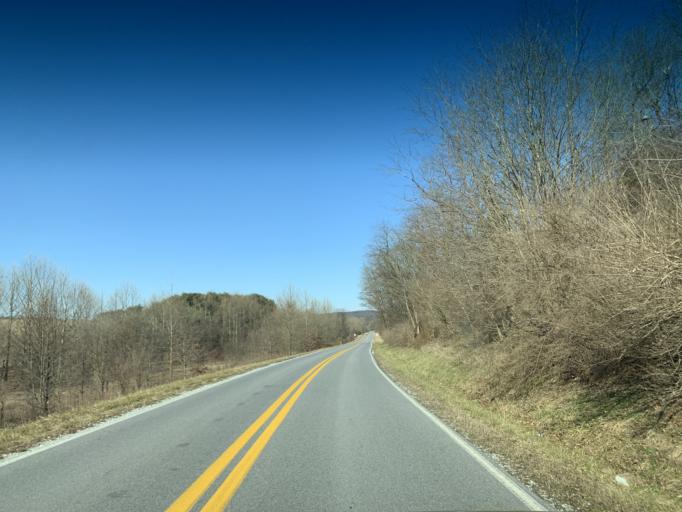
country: US
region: Maryland
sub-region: Carroll County
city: Westminster
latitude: 39.6435
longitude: -76.9641
